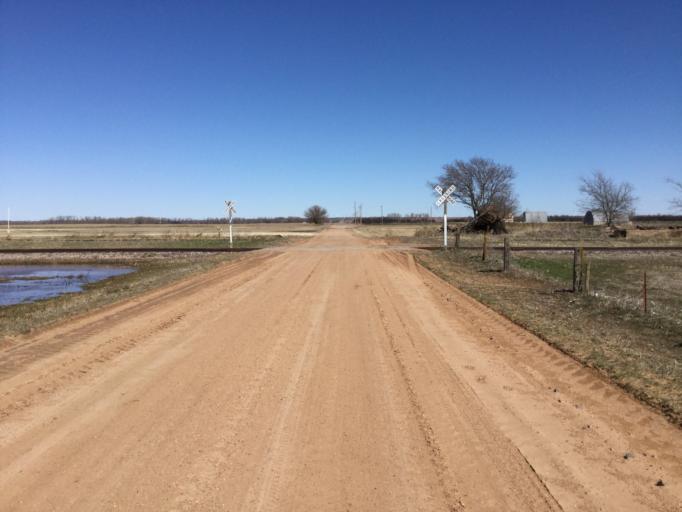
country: US
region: Kansas
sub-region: Barber County
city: Medicine Lodge
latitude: 37.2513
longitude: -98.5140
